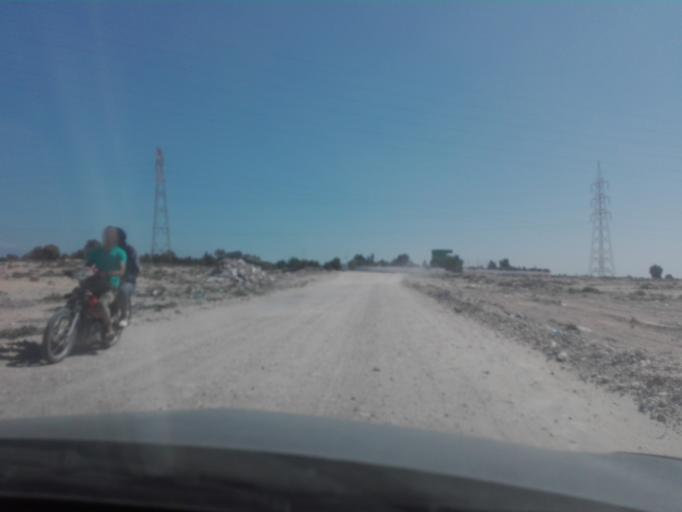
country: TN
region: Qabis
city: Gabes
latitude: 33.8737
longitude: 10.0304
